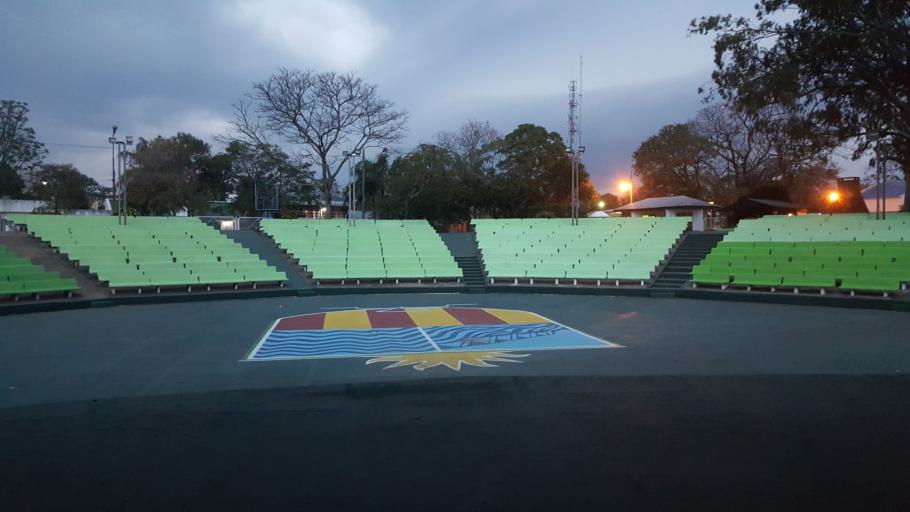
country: AR
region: Corrientes
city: Ituzaingo
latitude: -27.5850
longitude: -56.6916
